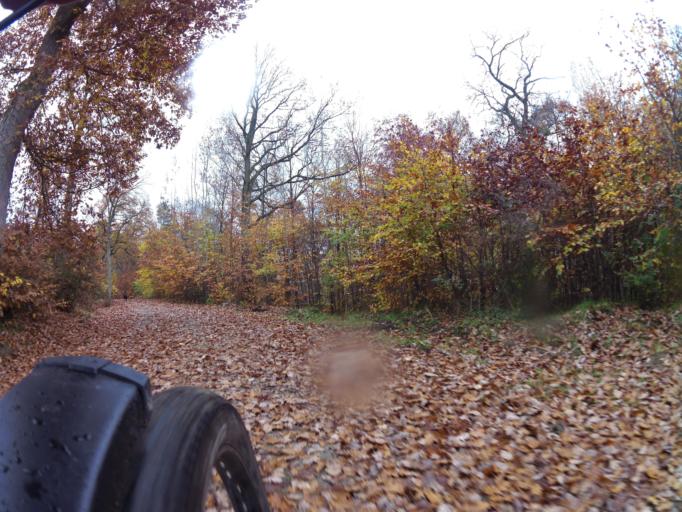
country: PL
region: Pomeranian Voivodeship
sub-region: Powiat wejherowski
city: Gniewino
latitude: 54.7558
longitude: 18.0814
